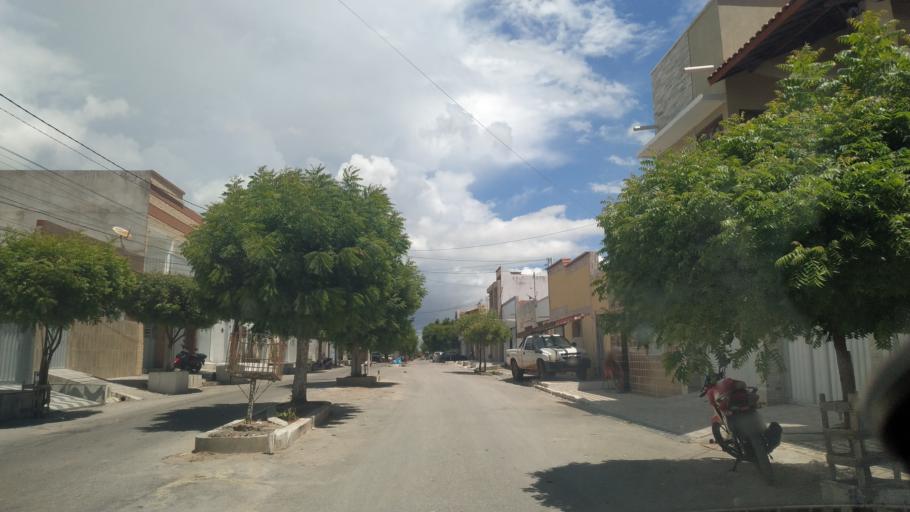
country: BR
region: Rio Grande do Norte
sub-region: Areia Branca
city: Areia Branca
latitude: -4.9511
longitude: -37.1336
